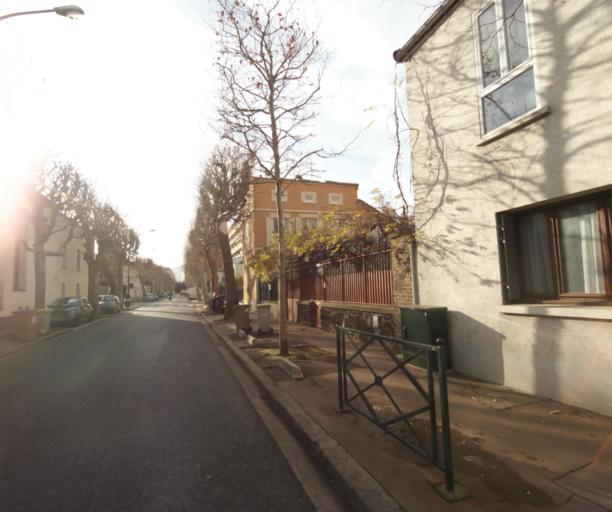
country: FR
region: Ile-de-France
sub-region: Departement des Hauts-de-Seine
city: Colombes
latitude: 48.9103
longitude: 2.2535
